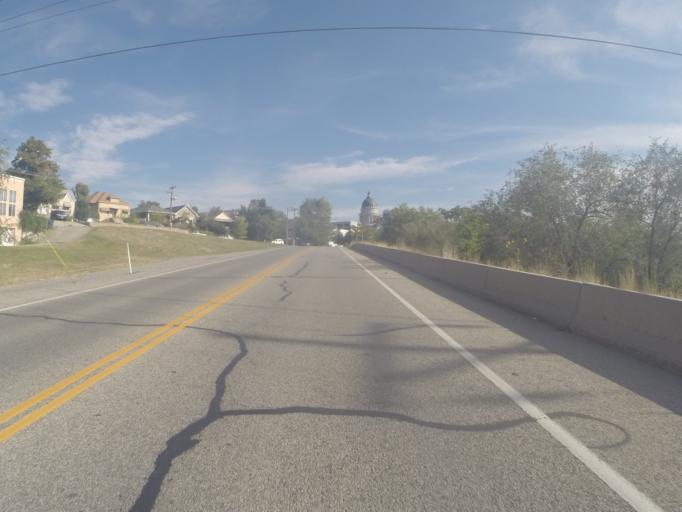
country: US
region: Utah
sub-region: Salt Lake County
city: Salt Lake City
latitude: 40.7816
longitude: -111.8909
